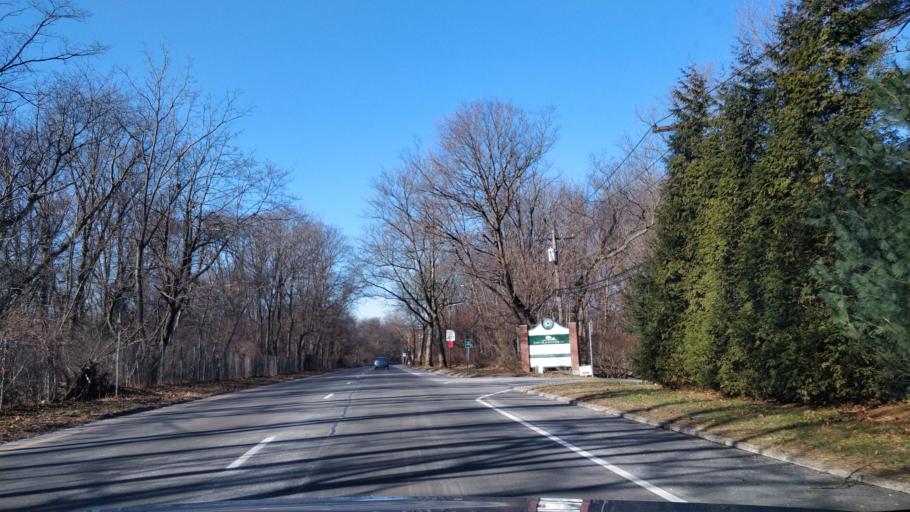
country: US
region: New York
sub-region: Nassau County
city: New Cassel
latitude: 40.7801
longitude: -73.5778
